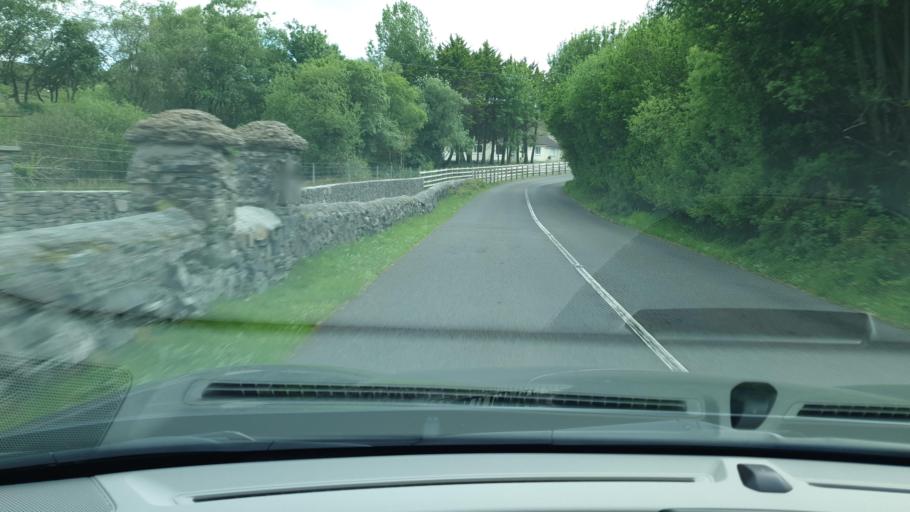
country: IE
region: Connaught
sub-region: County Galway
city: Clifden
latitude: 53.4569
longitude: -9.8207
